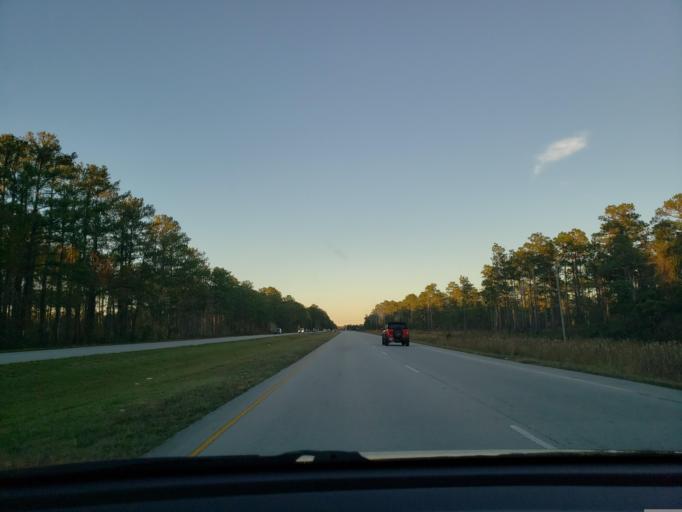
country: US
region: North Carolina
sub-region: Onslow County
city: Jacksonville
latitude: 34.6502
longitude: -77.4764
